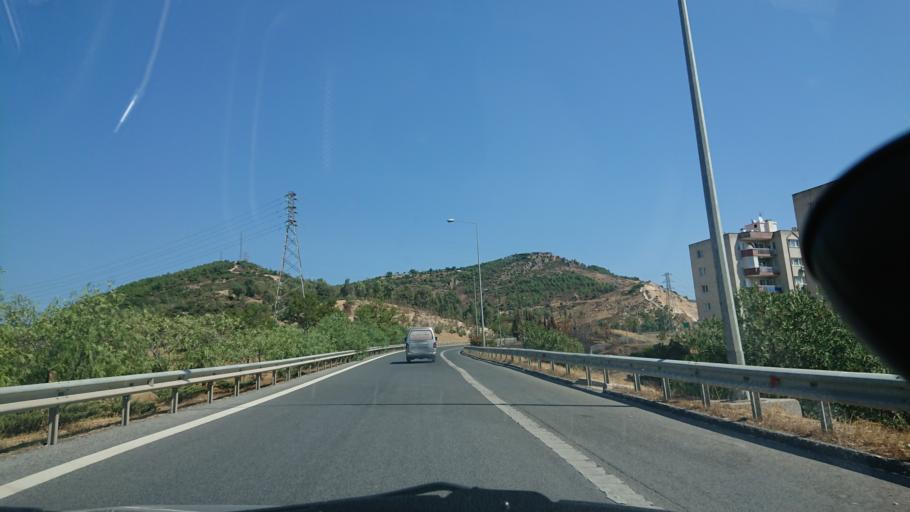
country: TR
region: Izmir
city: Karsiyaka
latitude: 38.4853
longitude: 27.1155
